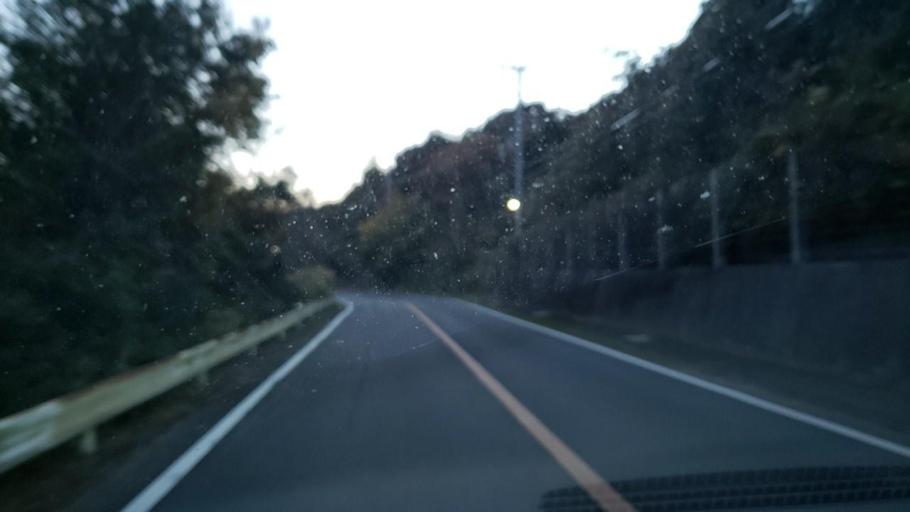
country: JP
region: Hyogo
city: Fukura
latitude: 34.2841
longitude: 134.7072
